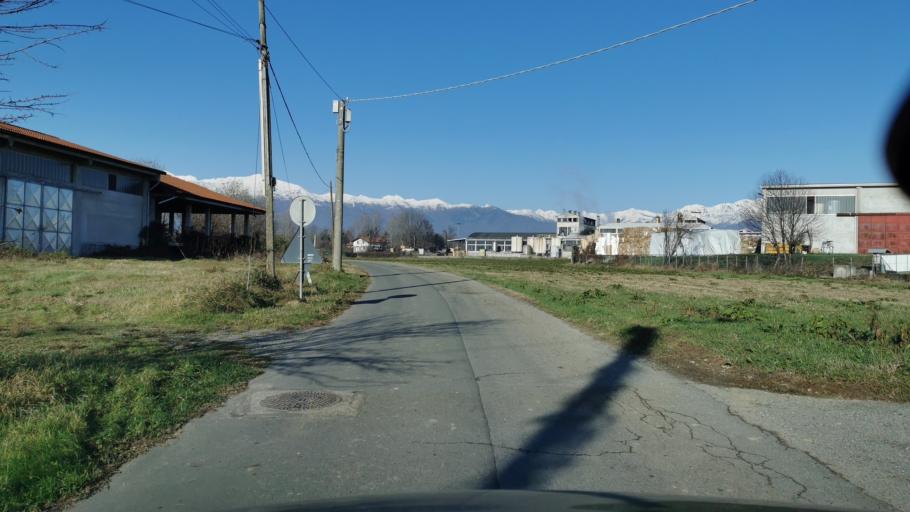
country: IT
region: Piedmont
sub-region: Provincia di Torino
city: Front
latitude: 45.2834
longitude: 7.6709
